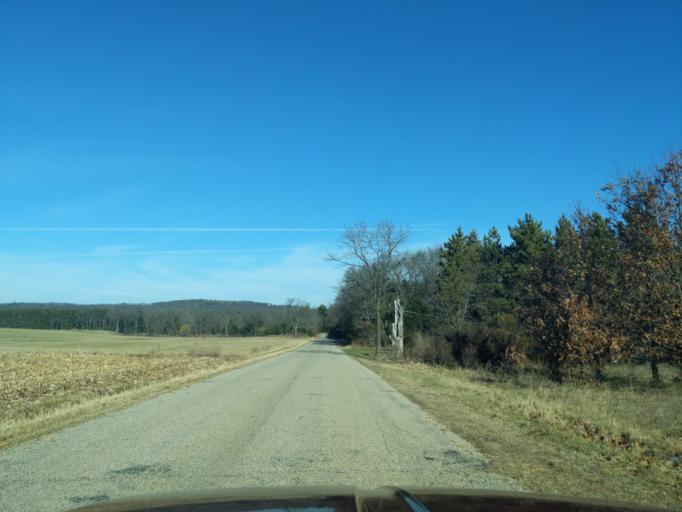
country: US
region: Wisconsin
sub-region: Waushara County
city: Silver Lake
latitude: 44.1011
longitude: -89.1789
